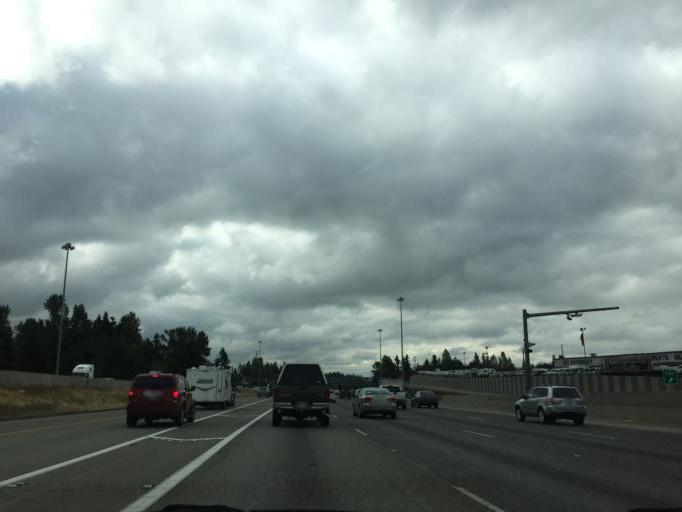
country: US
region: Washington
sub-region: King County
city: Lakeland South
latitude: 47.2830
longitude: -122.3091
